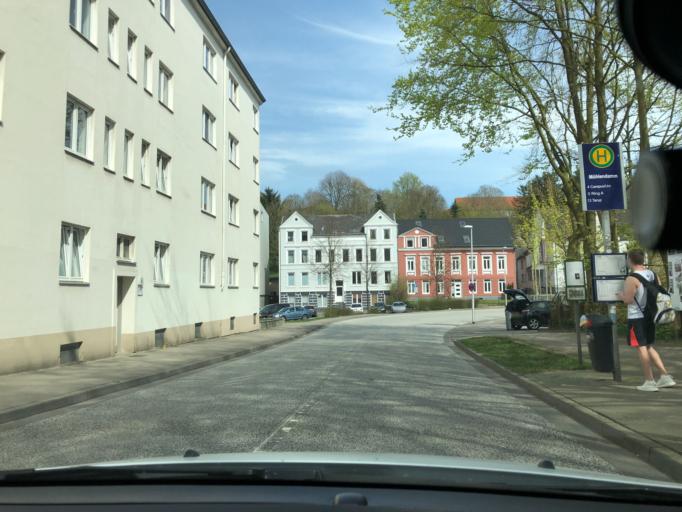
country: DE
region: Schleswig-Holstein
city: Flensburg
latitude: 54.7773
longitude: 9.4407
